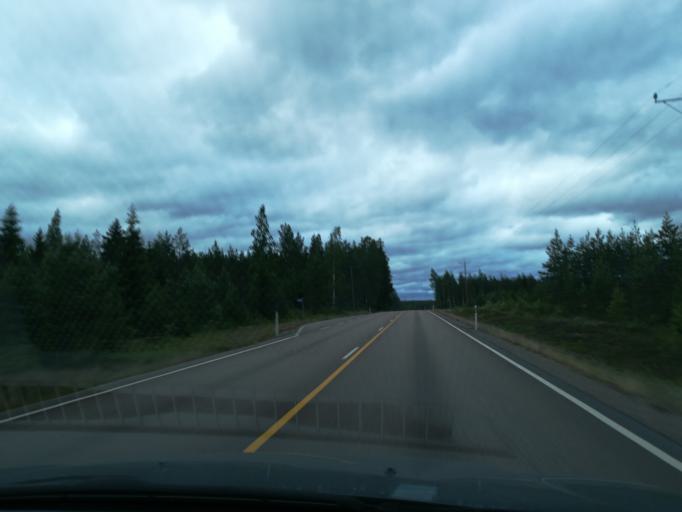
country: FI
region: Southern Savonia
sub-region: Mikkeli
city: Ristiina
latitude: 61.2965
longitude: 27.3927
